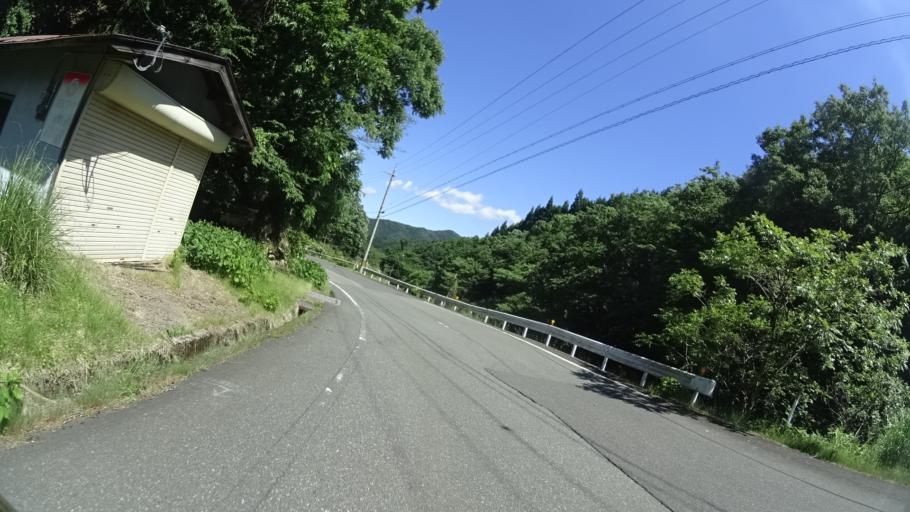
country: JP
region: Kyoto
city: Fukuchiyama
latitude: 35.4277
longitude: 135.0528
